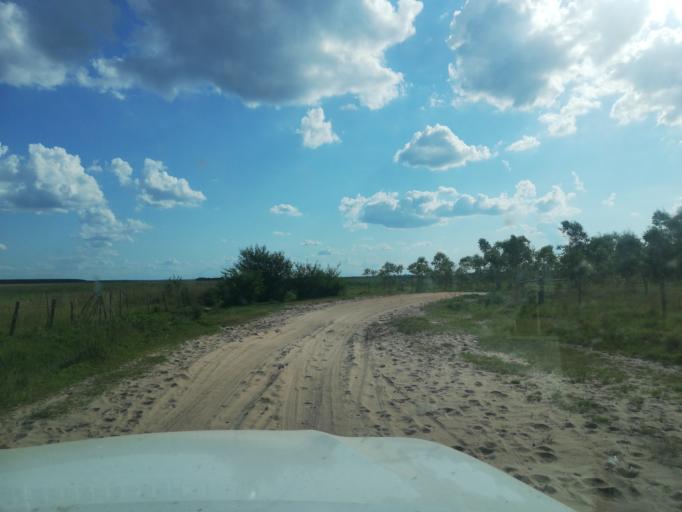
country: AR
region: Corrientes
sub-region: Departamento de San Miguel
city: San Miguel
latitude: -27.9912
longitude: -57.5654
